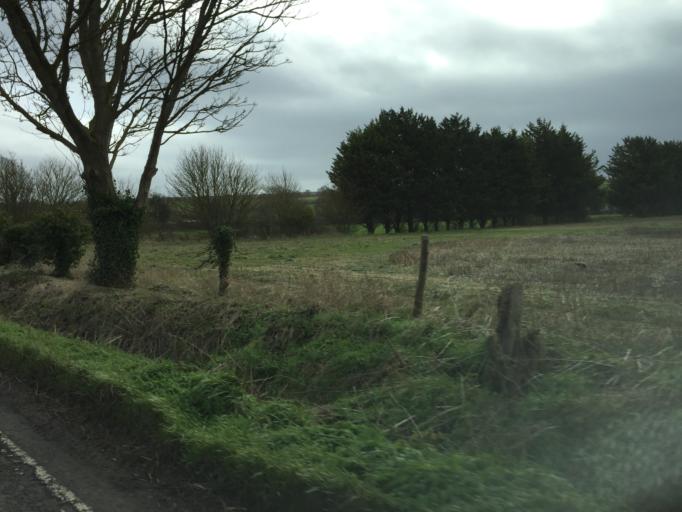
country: GB
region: England
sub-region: Oxfordshire
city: Blewbury
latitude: 51.5684
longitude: -1.2444
